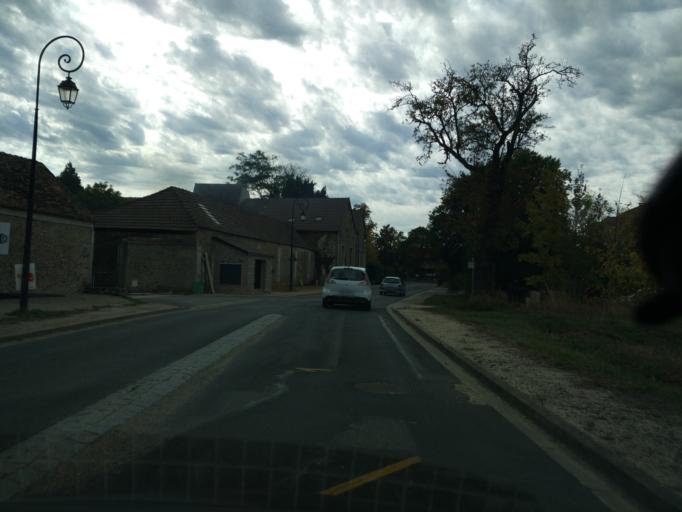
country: FR
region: Ile-de-France
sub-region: Departement de l'Essonne
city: Briis-sous-Forges
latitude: 48.6487
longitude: 2.1206
